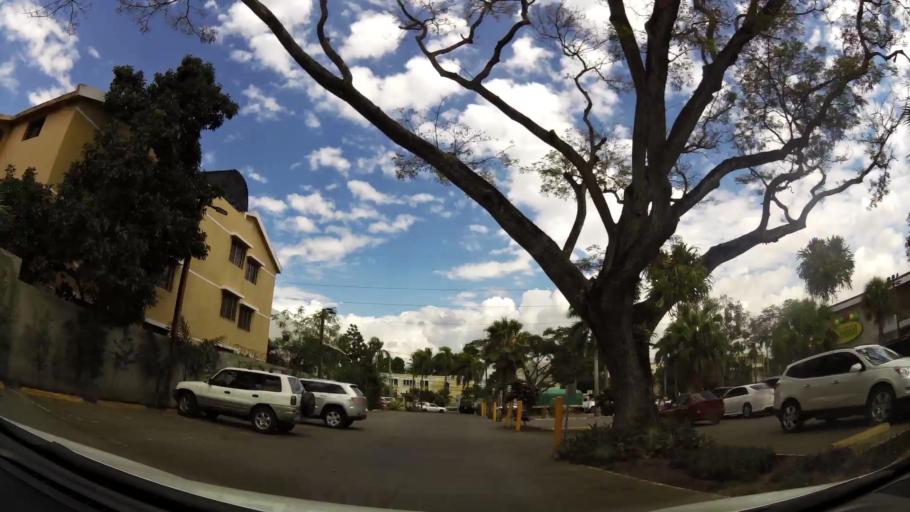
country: DO
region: Santiago
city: Santiago de los Caballeros
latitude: 19.4579
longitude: -70.6763
